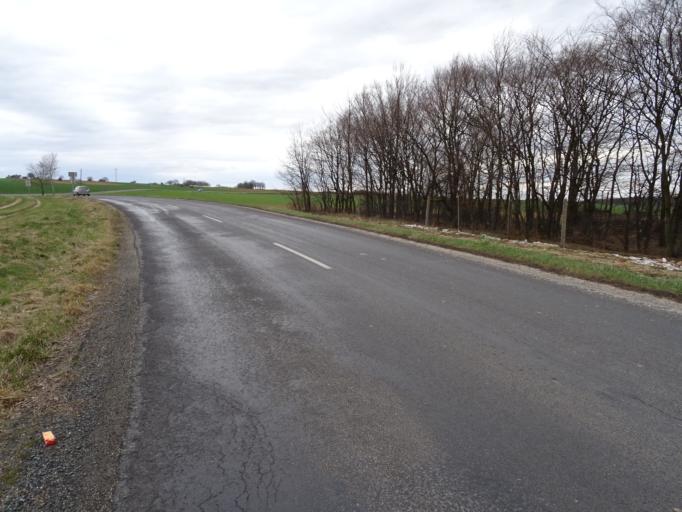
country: AT
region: Burgenland
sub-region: Politischer Bezirk Oberpullendorf
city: Lutzmannsburg
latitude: 47.4126
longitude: 16.6420
